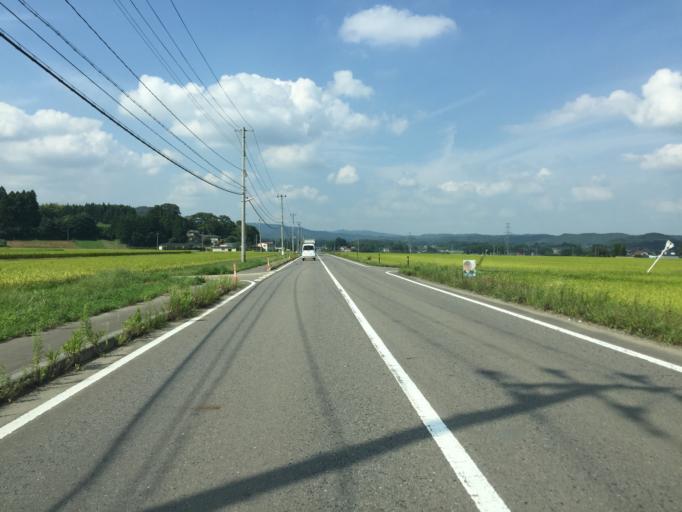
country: JP
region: Fukushima
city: Motomiya
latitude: 37.5514
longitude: 140.3841
